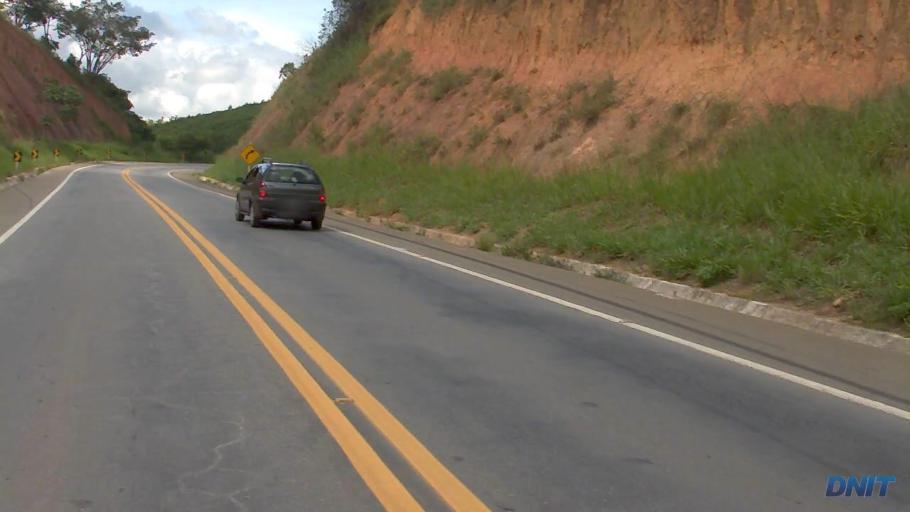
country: BR
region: Minas Gerais
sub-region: Belo Oriente
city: Belo Oriente
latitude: -19.0932
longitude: -42.1930
